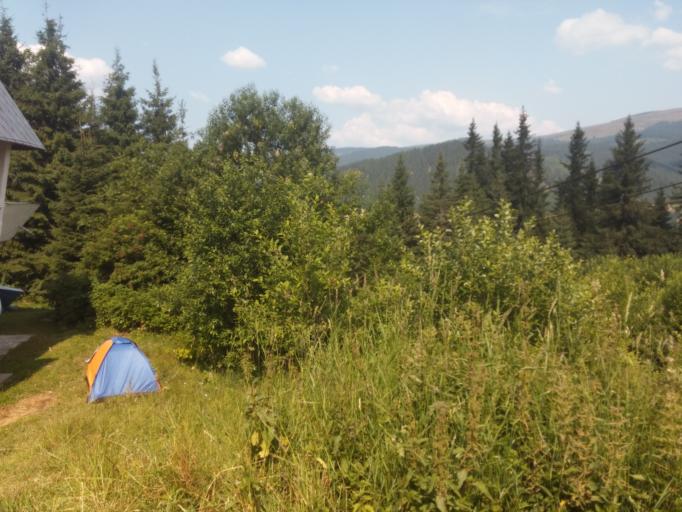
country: RO
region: Valcea
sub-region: Comuna Voineasa
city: Voineasa
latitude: 45.4299
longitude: 23.7581
